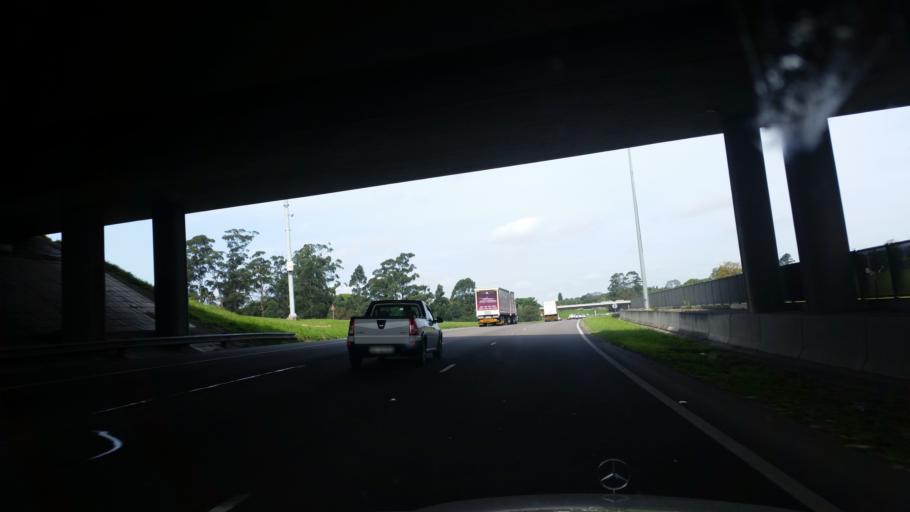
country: ZA
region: KwaZulu-Natal
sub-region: eThekwini Metropolitan Municipality
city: Berea
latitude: -29.8277
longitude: 30.8338
